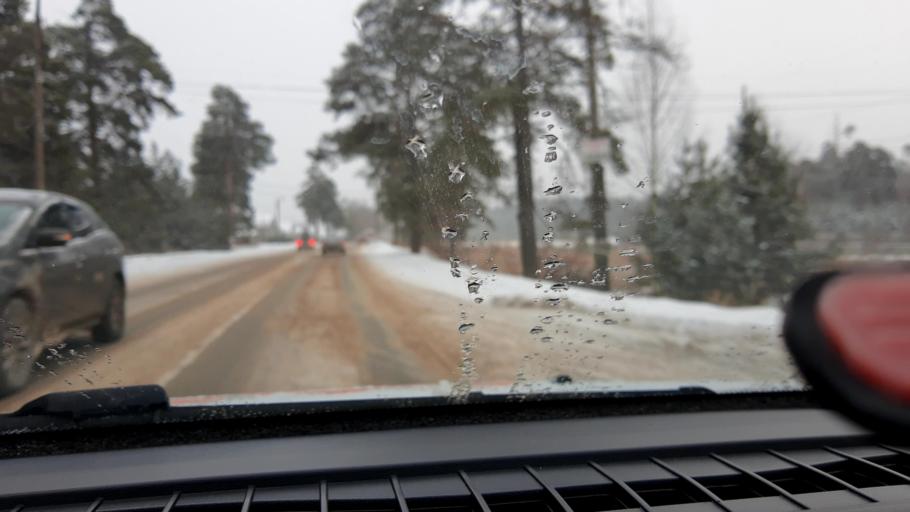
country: RU
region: Nizjnij Novgorod
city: Bor
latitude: 56.3292
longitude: 44.1240
